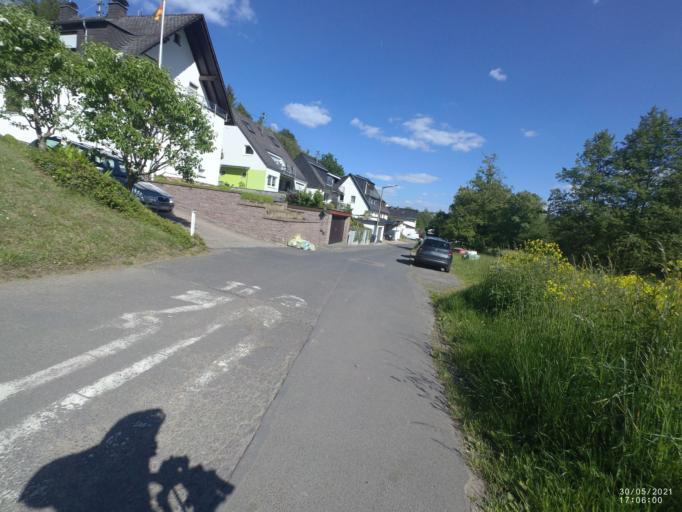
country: DE
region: Rheinland-Pfalz
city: Rhens
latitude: 50.2818
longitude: 7.6078
